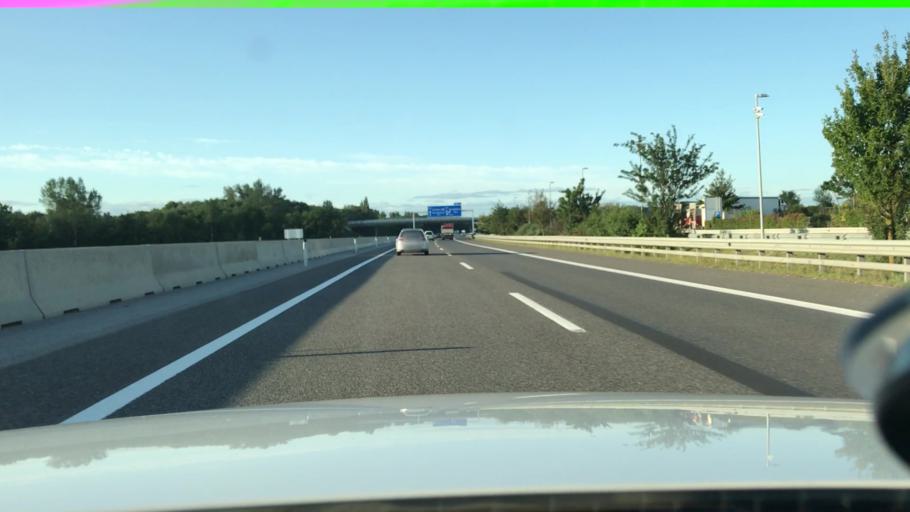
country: AT
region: Lower Austria
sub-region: Politischer Bezirk Sankt Polten
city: Herzogenburg
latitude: 48.3108
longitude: 15.7152
